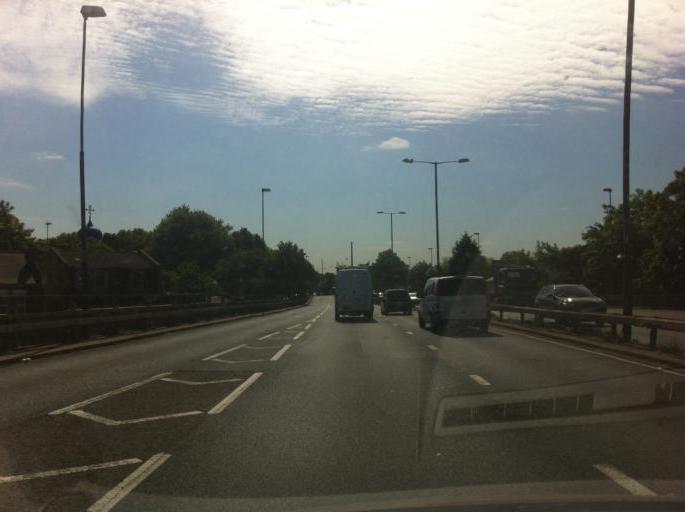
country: GB
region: England
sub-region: Greater London
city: Acton
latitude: 51.4920
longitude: -0.2831
